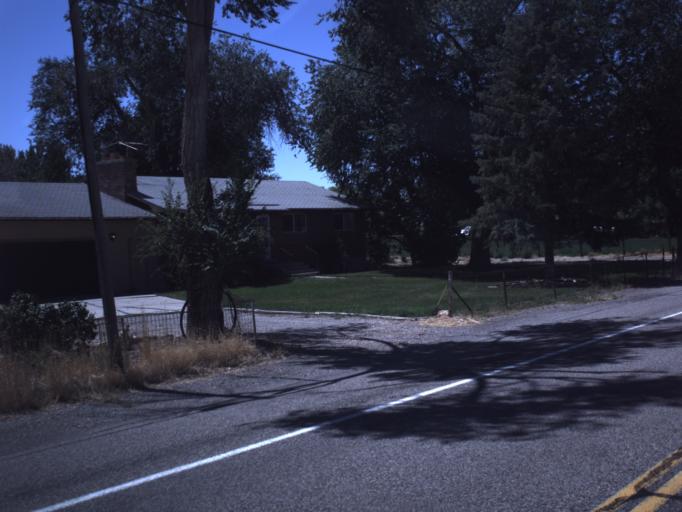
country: US
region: Utah
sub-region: Millard County
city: Delta
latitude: 39.5339
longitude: -112.2957
